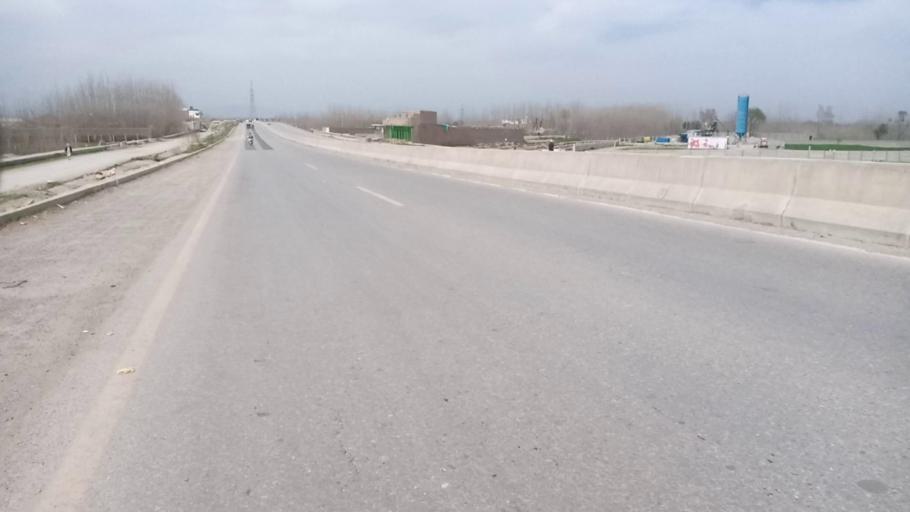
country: PK
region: Khyber Pakhtunkhwa
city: Peshawar
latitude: 34.0508
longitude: 71.6136
